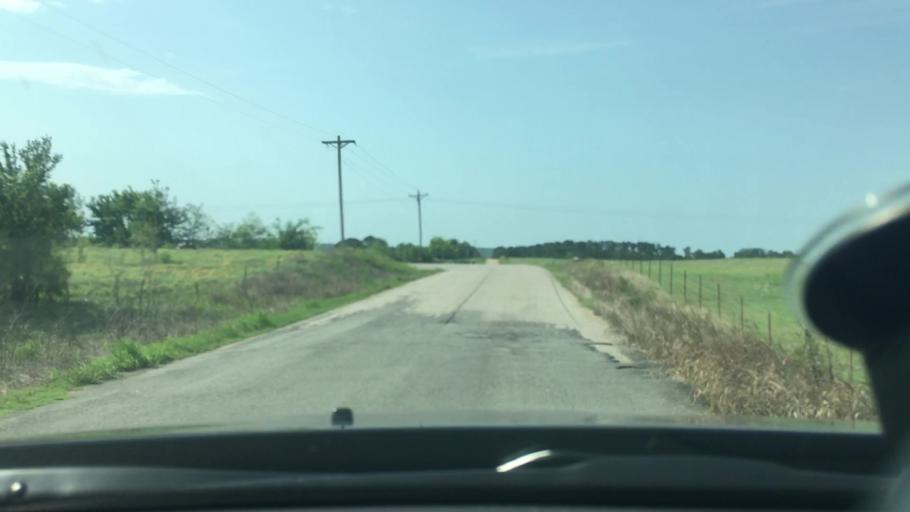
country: US
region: Oklahoma
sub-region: Atoka County
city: Atoka
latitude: 34.4625
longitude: -96.0407
